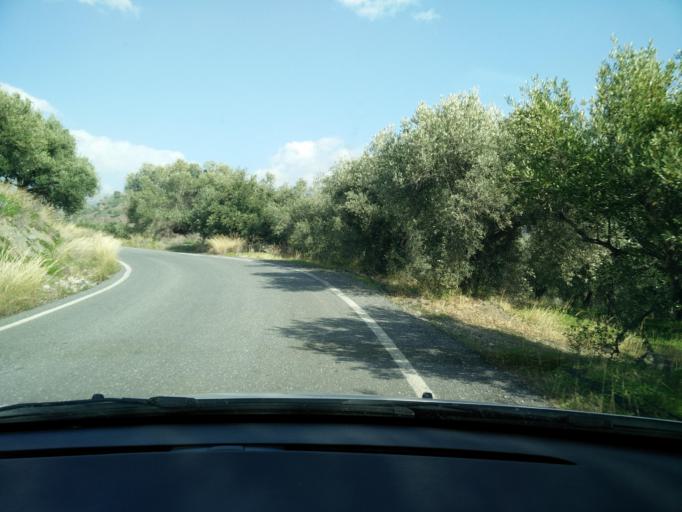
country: GR
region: Crete
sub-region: Nomos Lasithiou
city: Gra Liyia
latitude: 35.0314
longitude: 25.5809
